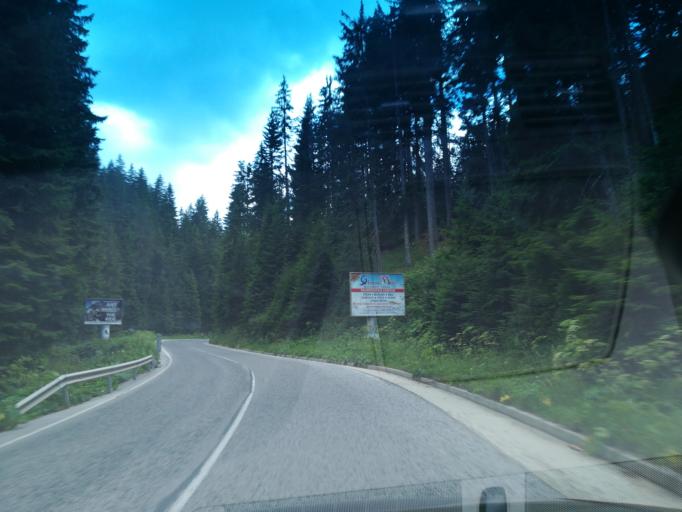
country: BG
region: Smolyan
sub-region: Obshtina Chepelare
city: Chepelare
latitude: 41.6689
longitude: 24.7144
